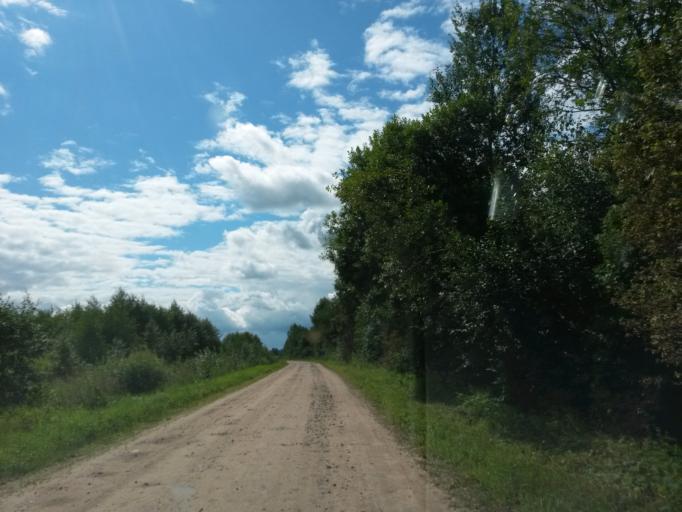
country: RU
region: Jaroslavl
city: Tutayev
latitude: 57.9445
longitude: 39.4493
